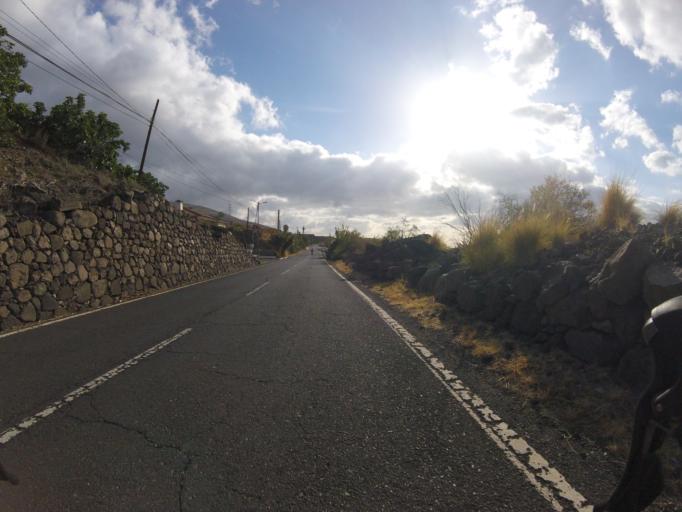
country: ES
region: Canary Islands
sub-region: Provincia de Santa Cruz de Tenerife
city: Candelaria
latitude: 28.3730
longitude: -16.3715
